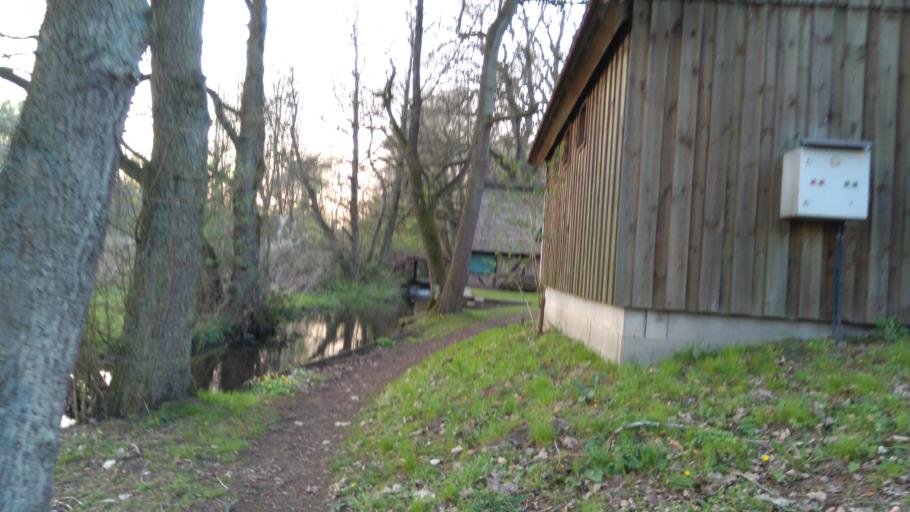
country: DE
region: Lower Saxony
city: Bargstedt
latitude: 53.4585
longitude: 9.4669
